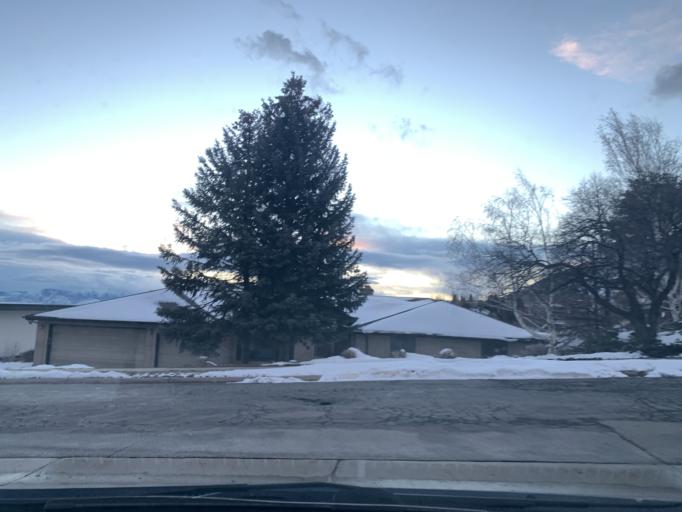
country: US
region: Utah
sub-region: Salt Lake County
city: Salt Lake City
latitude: 40.7845
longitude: -111.8521
